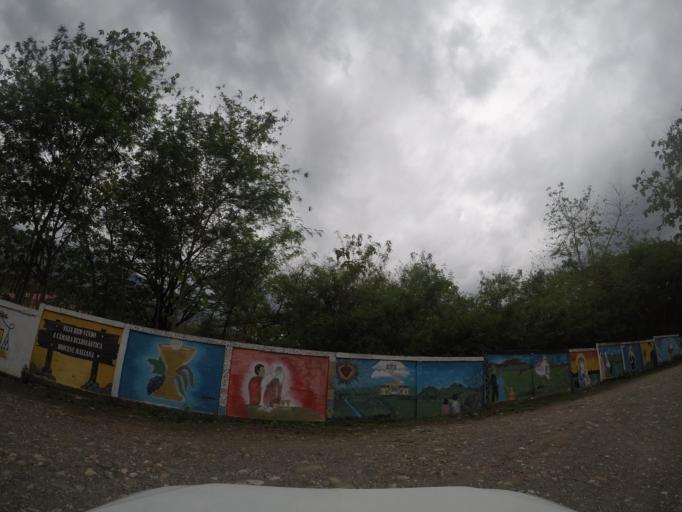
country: TL
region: Bobonaro
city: Maliana
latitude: -8.9728
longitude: 125.2233
